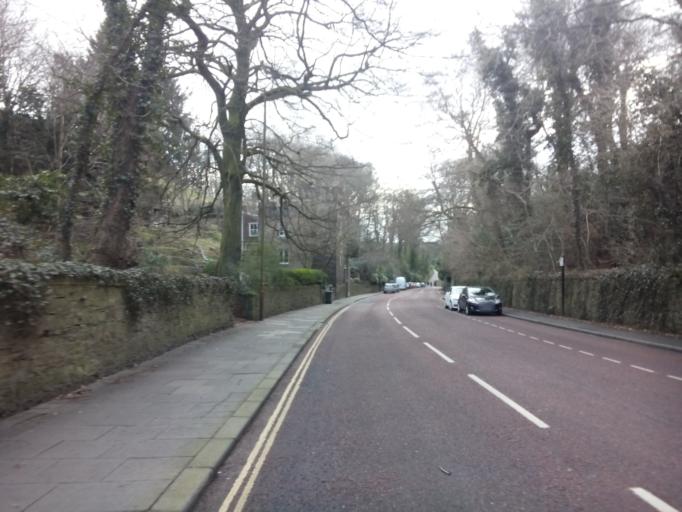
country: GB
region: England
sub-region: County Durham
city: Durham
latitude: 54.7816
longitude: -1.5855
